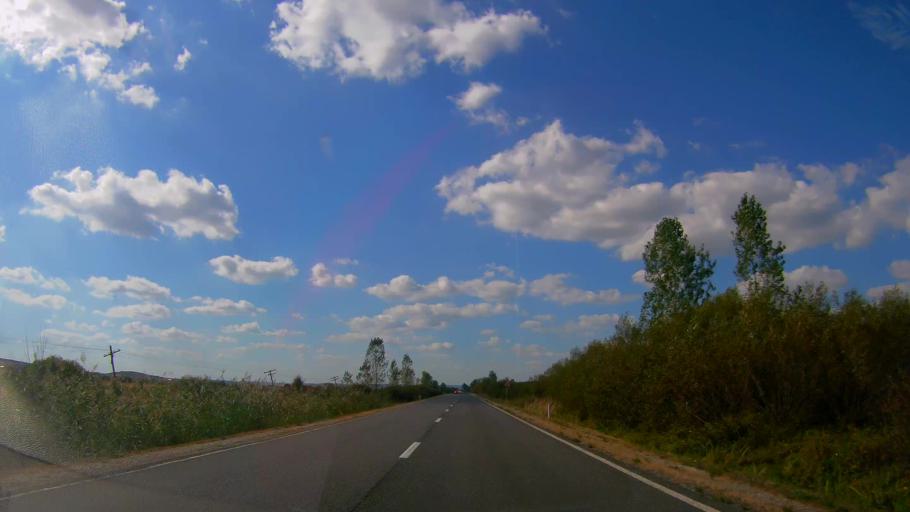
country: RO
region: Salaj
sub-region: Comuna Sarmasag
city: Sarmasag
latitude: 47.3268
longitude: 22.8729
